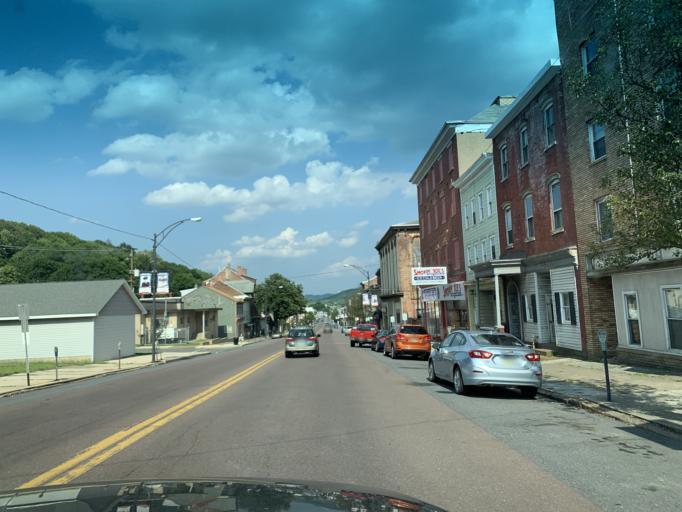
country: US
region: Pennsylvania
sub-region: Schuylkill County
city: Ashland
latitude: 40.7824
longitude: -76.3419
